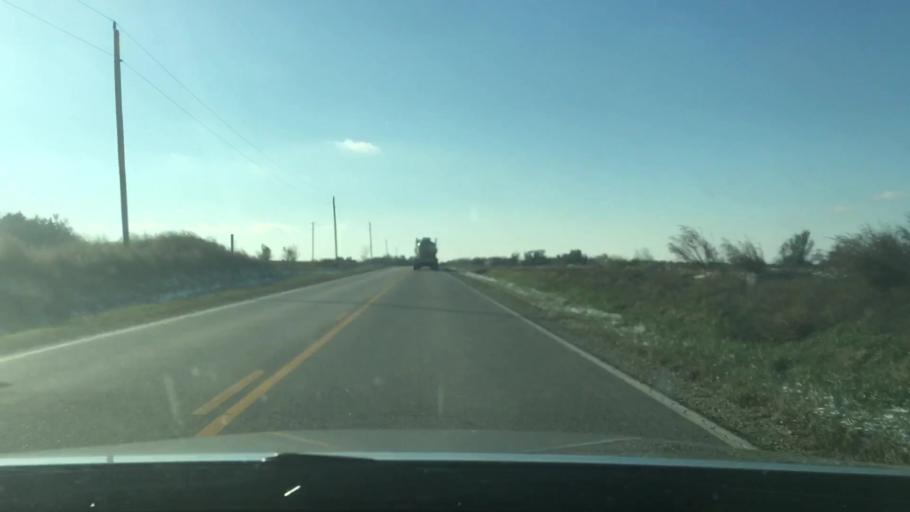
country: US
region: Kansas
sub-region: Rice County
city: Sterling
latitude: 38.1446
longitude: -98.1836
